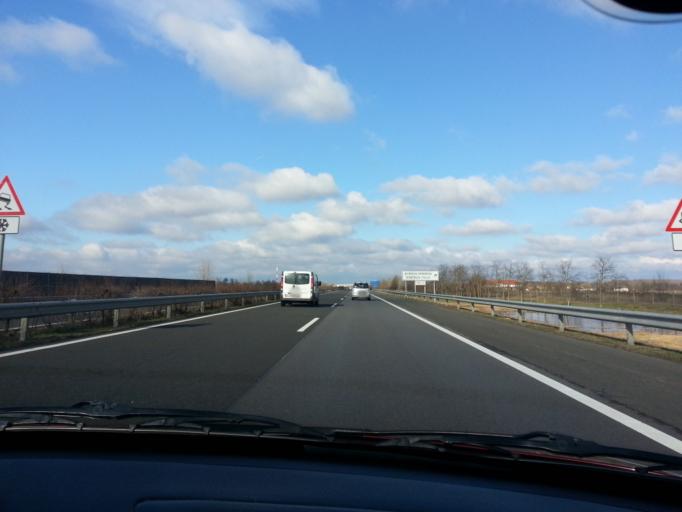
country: HU
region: Csongrad
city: Balastya
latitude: 46.3969
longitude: 19.9795
